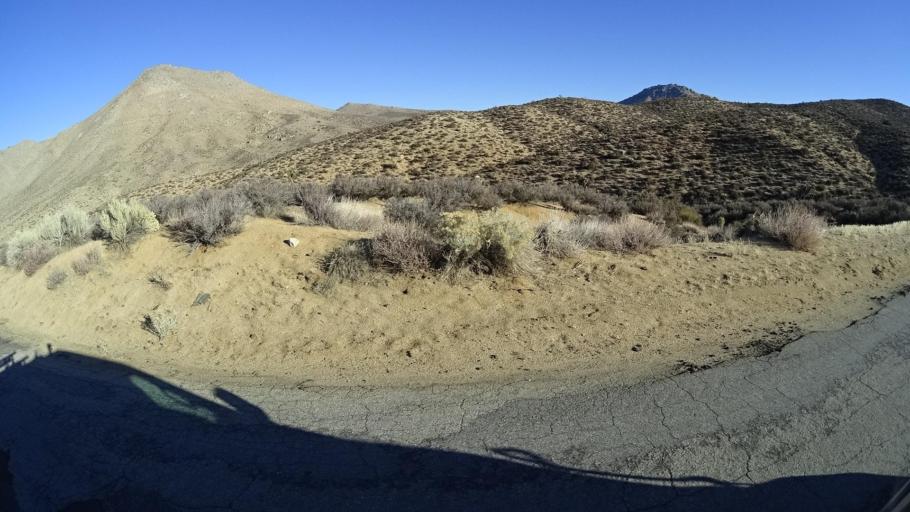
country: US
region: California
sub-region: Kern County
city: Weldon
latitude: 35.4572
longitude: -118.2161
